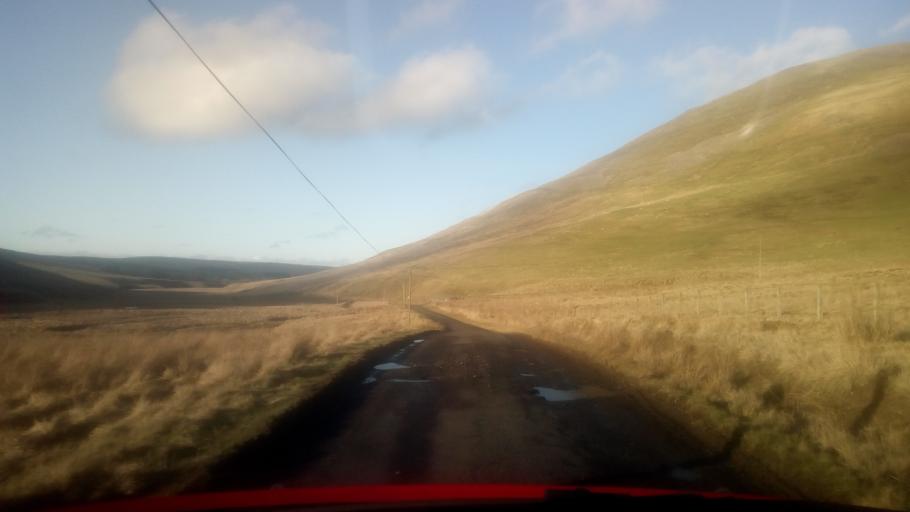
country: GB
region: England
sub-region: Northumberland
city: Rochester
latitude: 55.3994
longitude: -2.3777
